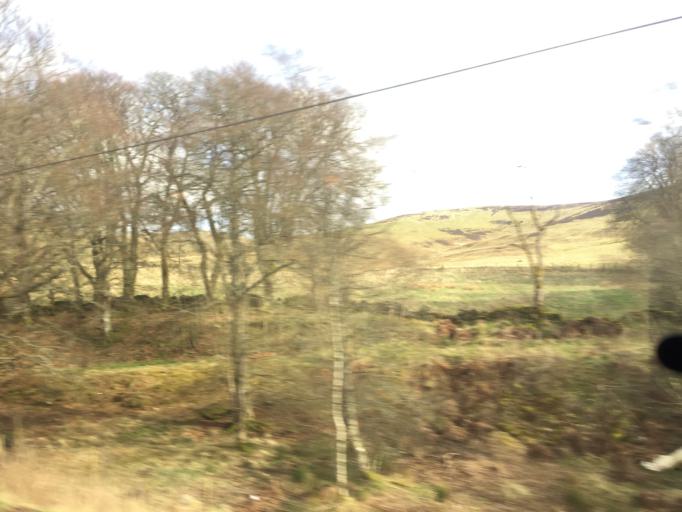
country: GB
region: Scotland
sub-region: South Lanarkshire
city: Douglas
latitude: 55.4869
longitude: -3.6885
